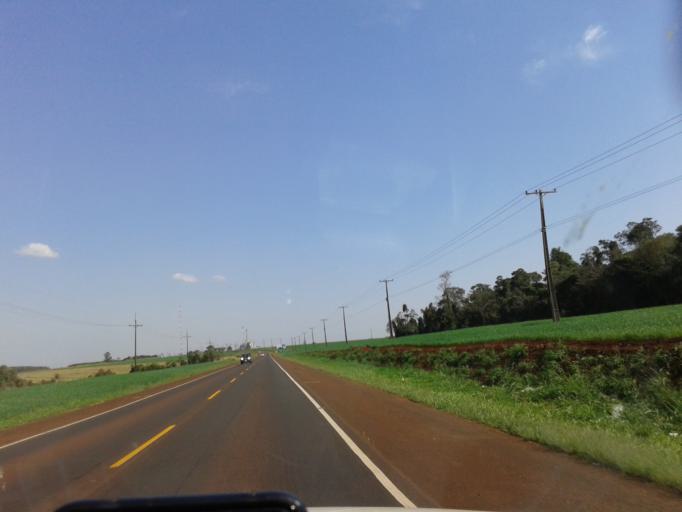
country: PY
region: Alto Parana
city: Colonia Yguazu
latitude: -25.6296
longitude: -54.9673
